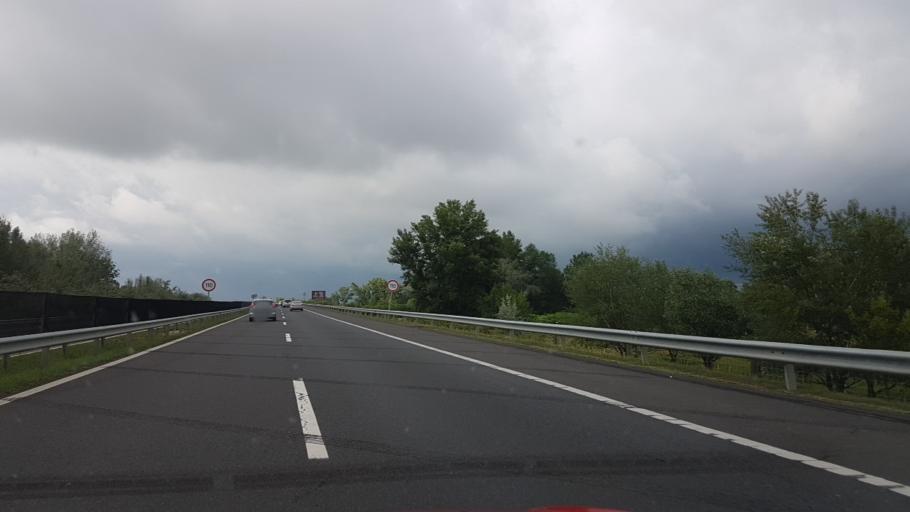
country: HU
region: Borsod-Abauj-Zemplen
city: Felsozsolca
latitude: 48.0836
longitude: 20.8508
